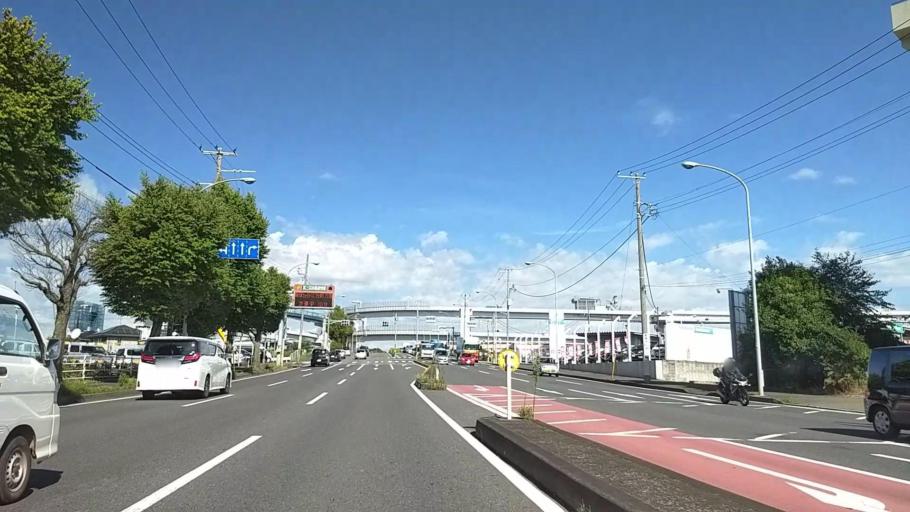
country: JP
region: Kanagawa
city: Yokohama
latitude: 35.5147
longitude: 139.5963
